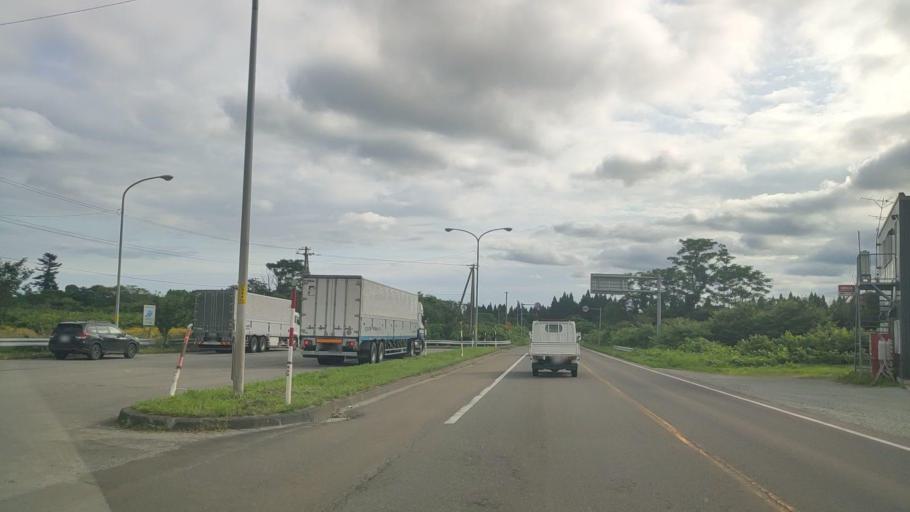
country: JP
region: Hokkaido
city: Niseko Town
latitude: 42.5903
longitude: 140.4507
